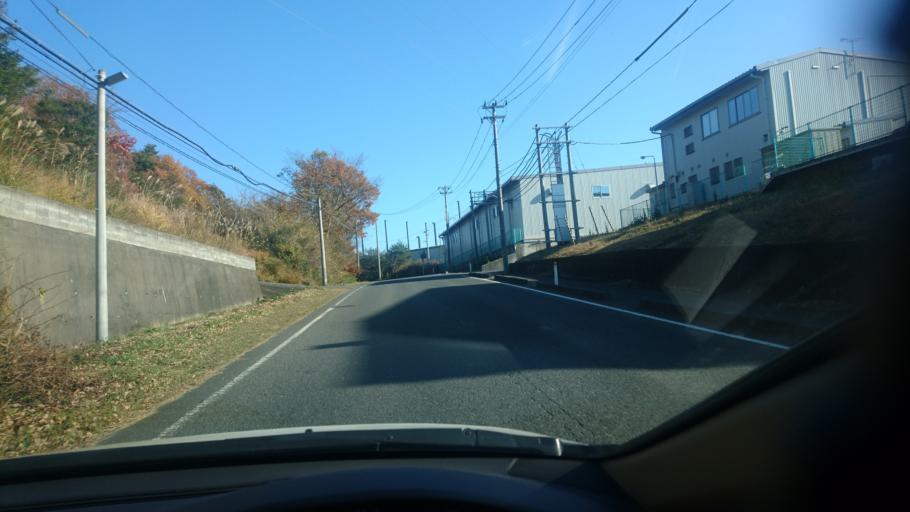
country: JP
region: Miyagi
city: Tomiya
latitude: 38.4541
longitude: 140.8945
